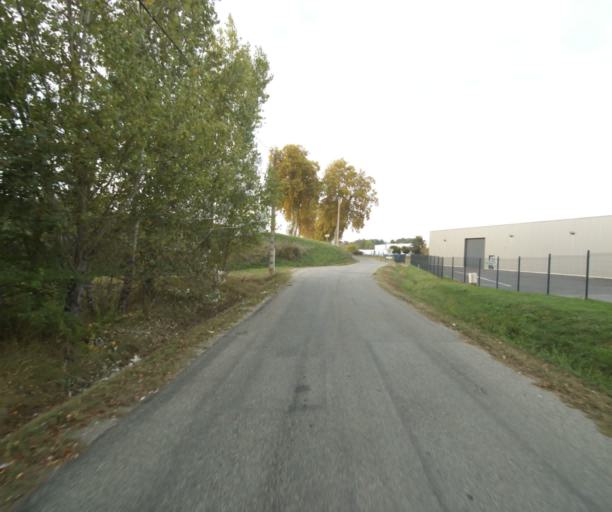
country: FR
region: Midi-Pyrenees
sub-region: Departement du Tarn-et-Garonne
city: Grisolles
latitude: 43.8390
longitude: 1.2948
